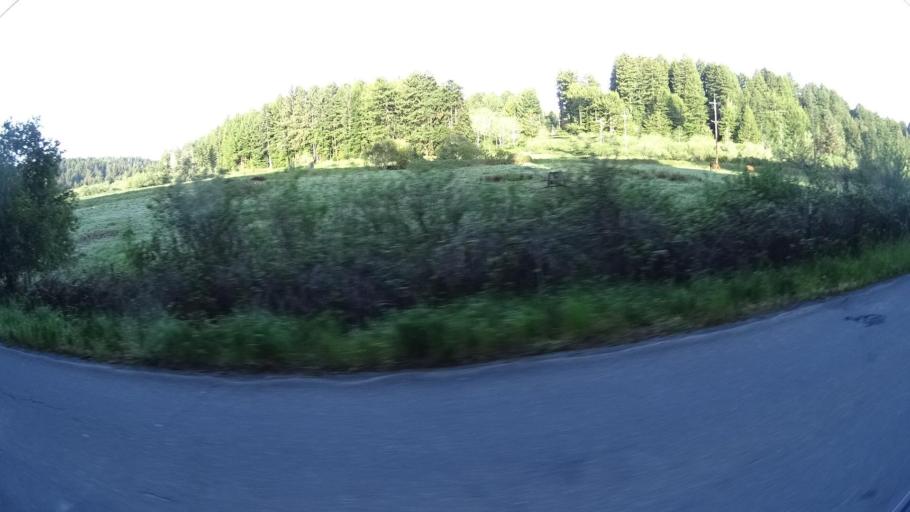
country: US
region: California
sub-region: Humboldt County
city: Myrtletown
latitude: 40.7803
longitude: -124.1180
